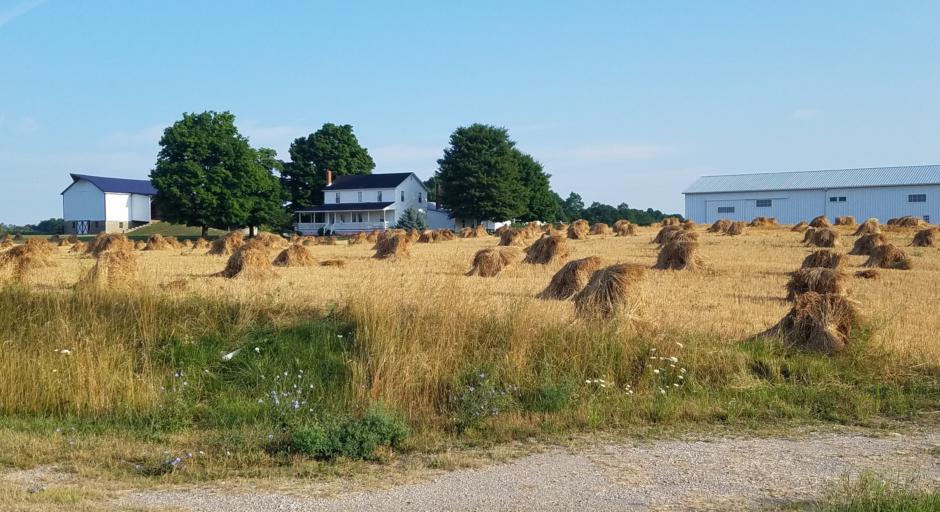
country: US
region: Ohio
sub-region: Richland County
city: Lexington
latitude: 40.5864
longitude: -82.5985
